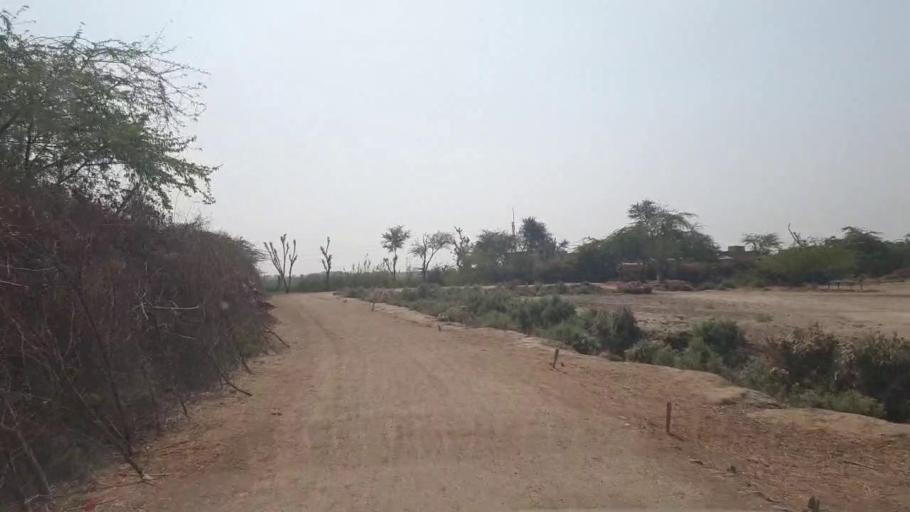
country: PK
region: Sindh
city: Dhoro Naro
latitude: 25.4652
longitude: 69.6129
